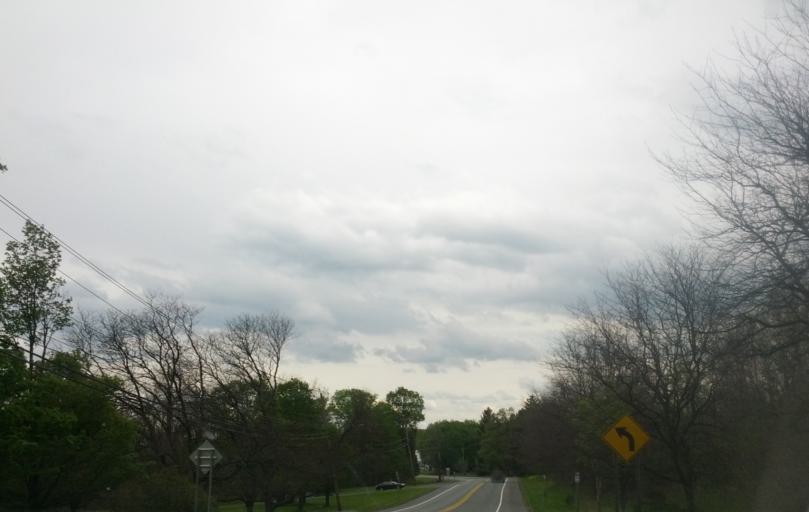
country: US
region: New York
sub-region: Onondaga County
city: Nedrow
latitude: 42.9936
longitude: -76.0963
